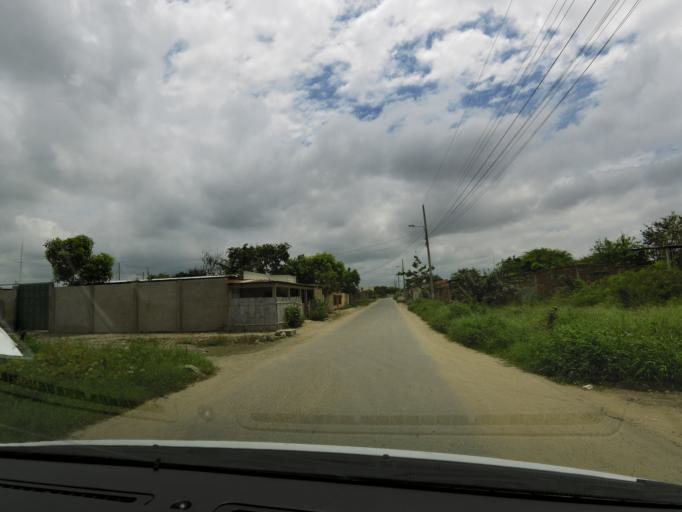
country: EC
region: El Oro
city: Huaquillas
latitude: -3.4857
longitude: -80.2096
